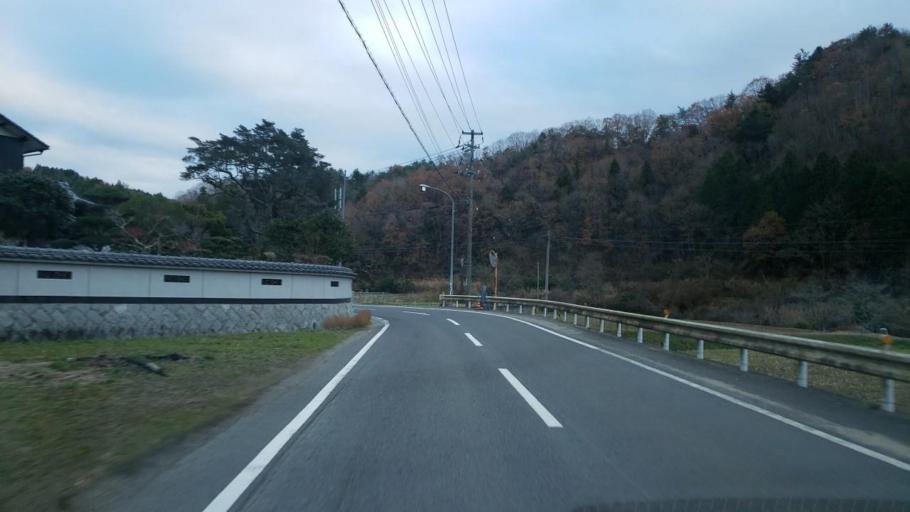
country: JP
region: Tokushima
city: Wakimachi
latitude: 34.1760
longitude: 134.1878
